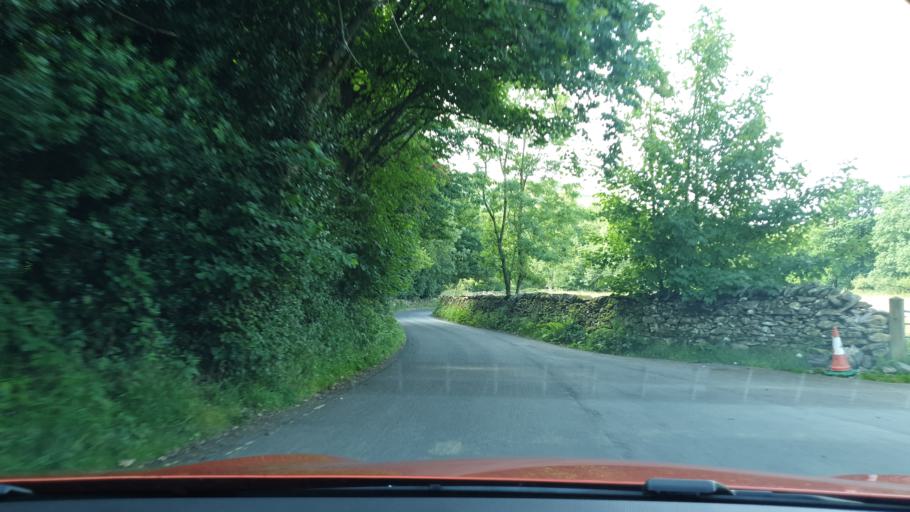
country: GB
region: England
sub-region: Cumbria
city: Penrith
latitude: 54.5708
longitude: -2.8616
